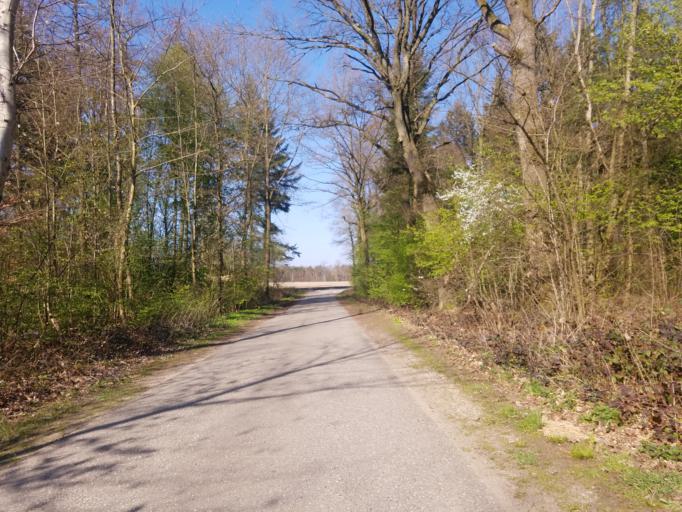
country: DE
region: Baden-Wuerttemberg
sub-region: Karlsruhe Region
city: Schwarzach
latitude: 48.7556
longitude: 8.0689
